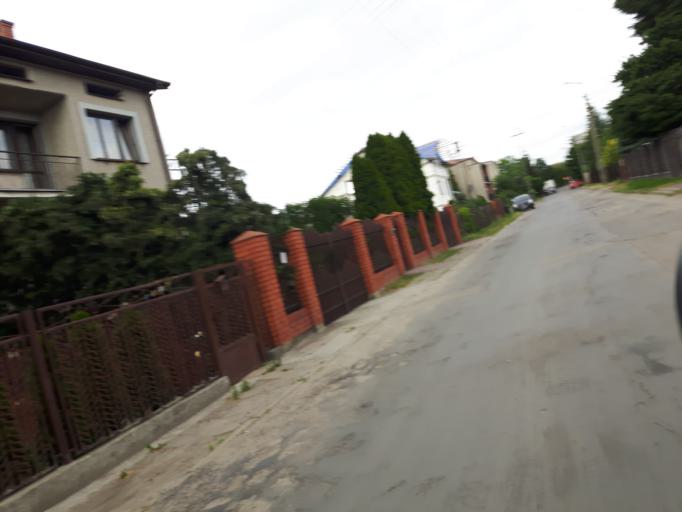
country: PL
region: Masovian Voivodeship
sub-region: Powiat wolominski
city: Zabki
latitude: 52.2827
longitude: 21.1081
